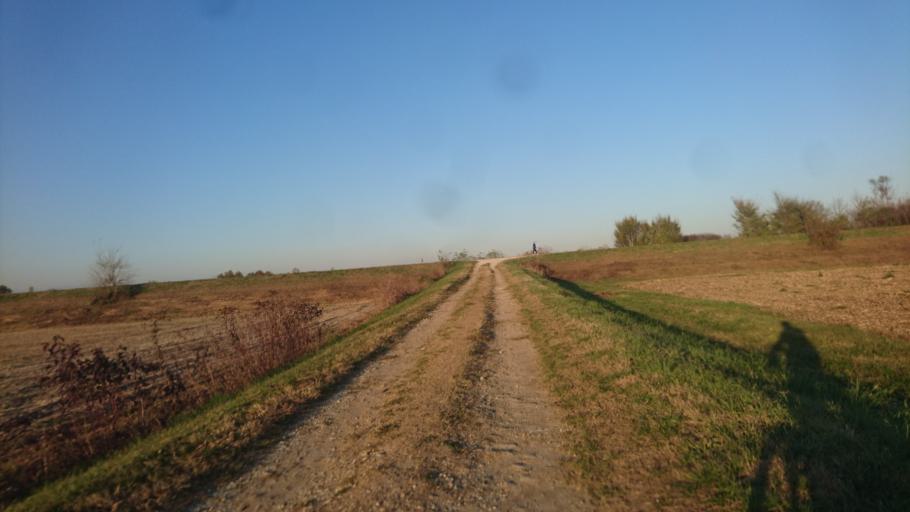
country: IT
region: Veneto
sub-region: Provincia di Padova
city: Saccolongo
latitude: 45.3995
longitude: 11.7719
